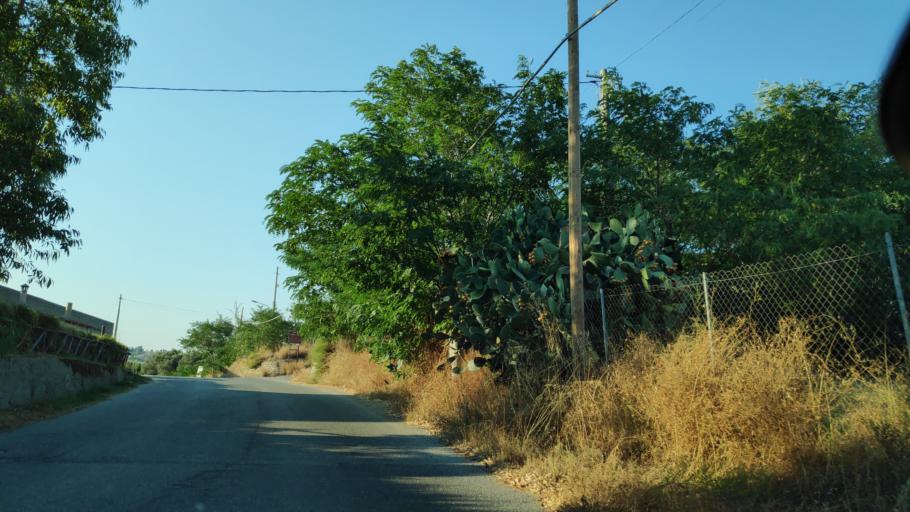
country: IT
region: Calabria
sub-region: Provincia di Reggio Calabria
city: Monasterace Marina
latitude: 38.4469
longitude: 16.5766
